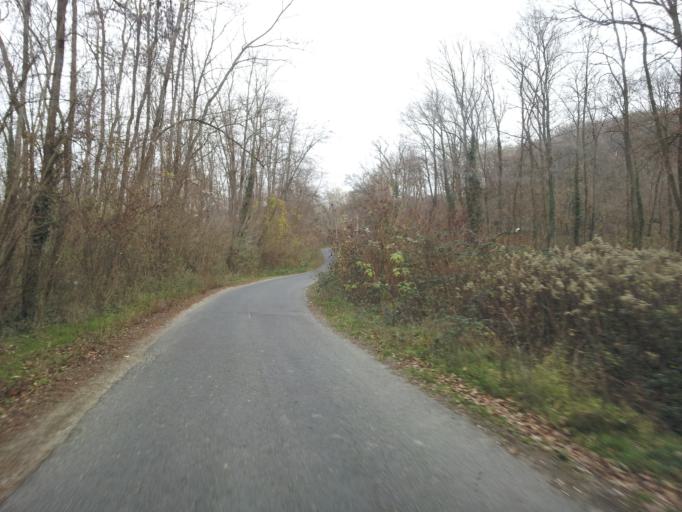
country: HU
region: Zala
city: Cserszegtomaj
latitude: 46.8459
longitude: 17.2023
